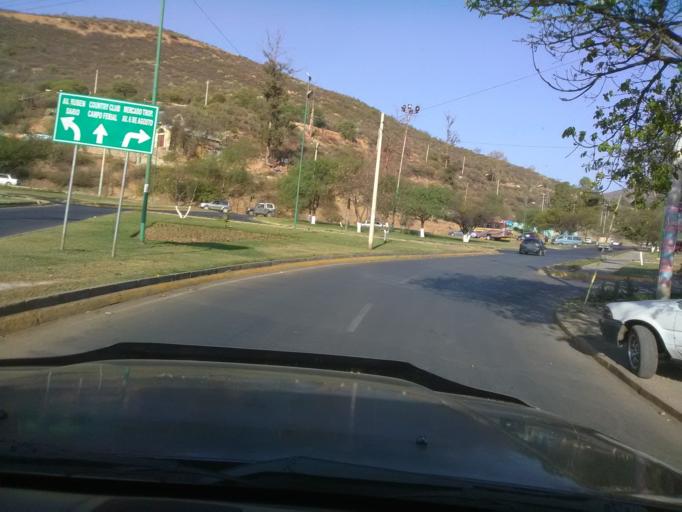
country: BO
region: Cochabamba
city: Cochabamba
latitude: -17.3983
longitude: -66.1364
